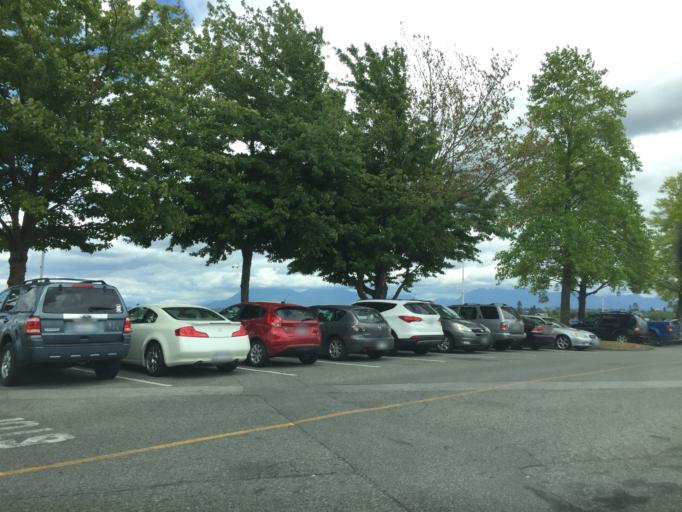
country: CA
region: British Columbia
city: Richmond
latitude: 49.1795
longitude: -123.1529
